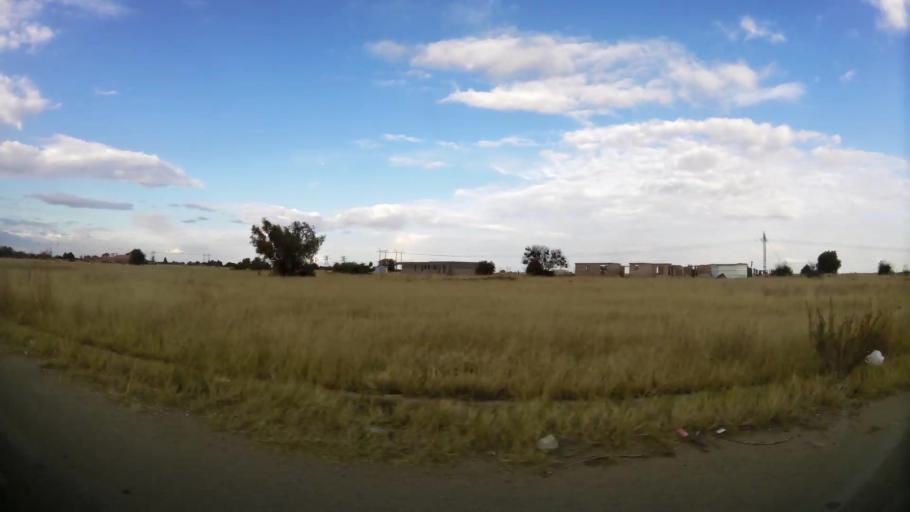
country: ZA
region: Orange Free State
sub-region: Lejweleputswa District Municipality
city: Welkom
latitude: -28.0051
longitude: 26.7330
